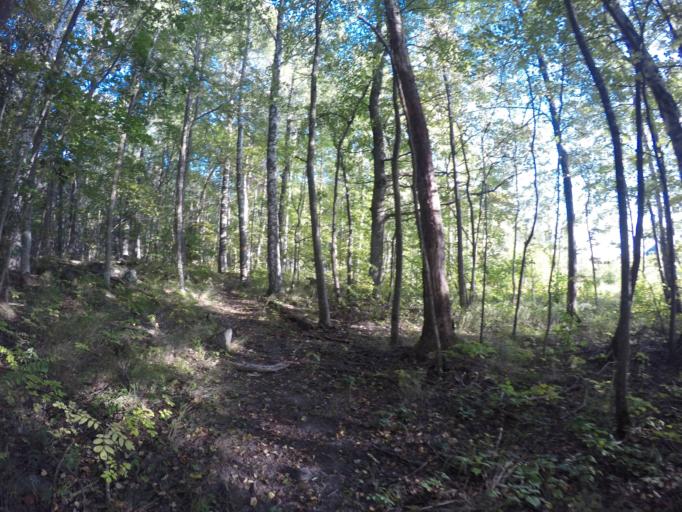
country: SE
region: Vaestmanland
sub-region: Hallstahammars Kommun
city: Kolback
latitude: 59.4752
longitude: 16.2293
